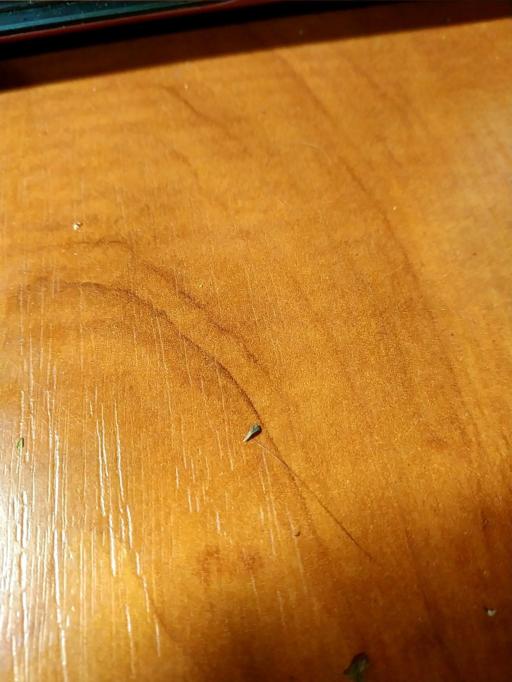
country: RU
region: Smolensk
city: Verkhnedneprovskiy
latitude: 55.0476
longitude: 33.2795
